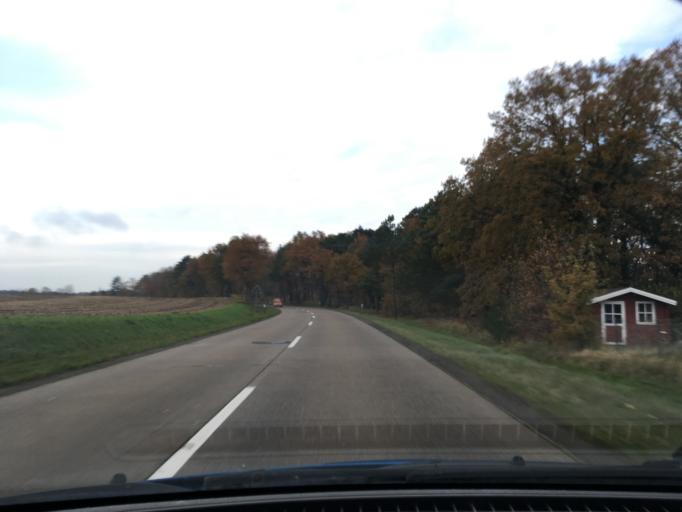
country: DE
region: Lower Saxony
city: Embsen
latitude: 53.1902
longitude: 10.3275
